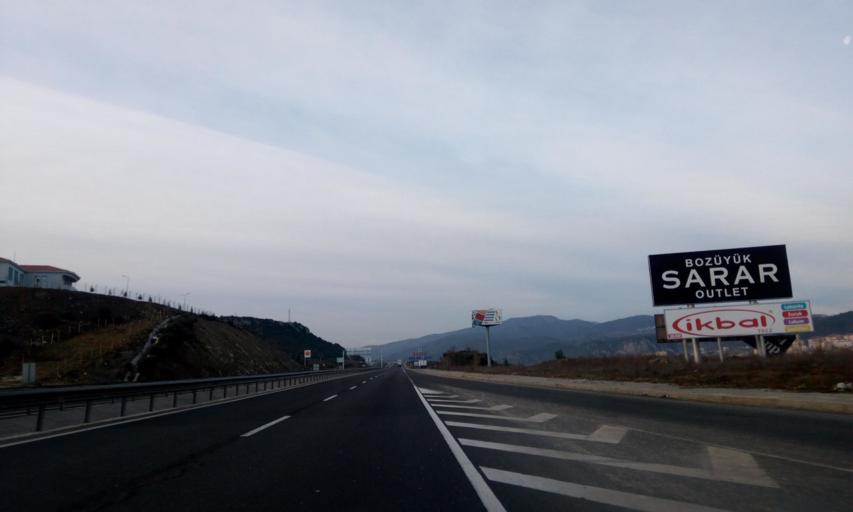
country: TR
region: Bilecik
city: Kuplu
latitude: 40.1343
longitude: 30.0206
